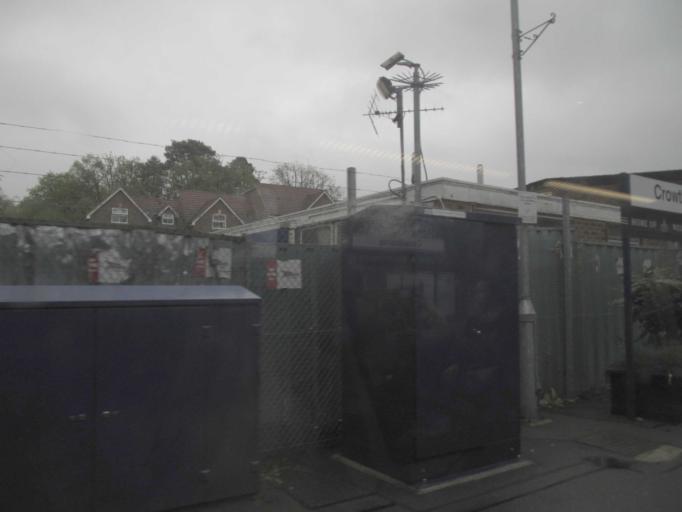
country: GB
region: England
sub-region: Hampshire
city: Yateley
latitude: 51.3668
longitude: -0.8191
